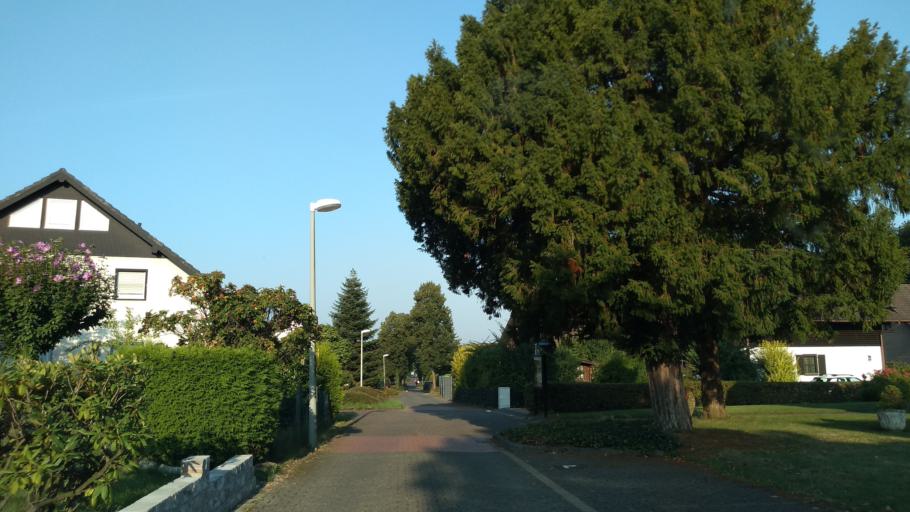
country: DE
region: North Rhine-Westphalia
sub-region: Regierungsbezirk Koln
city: Stossdorf
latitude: 50.8253
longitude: 7.2722
